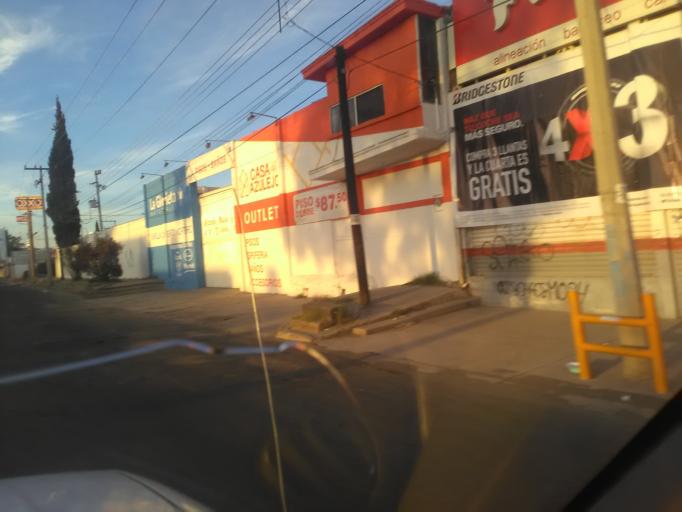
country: MX
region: Durango
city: Victoria de Durango
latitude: 23.9926
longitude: -104.6635
